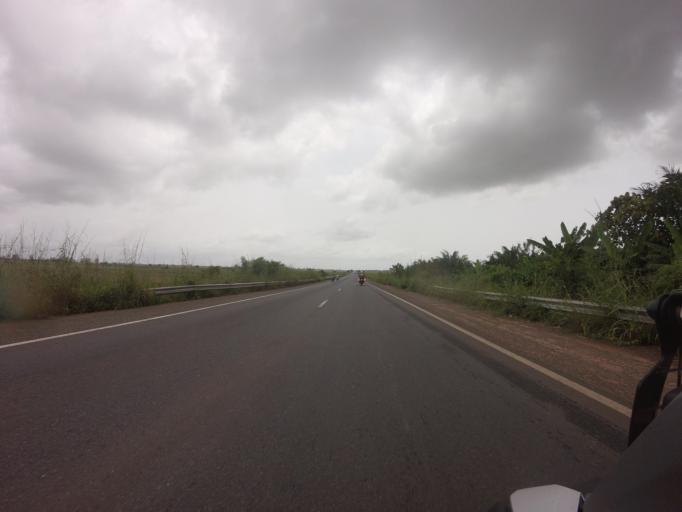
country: GH
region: Volta
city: Keta
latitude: 6.0637
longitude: 0.9219
